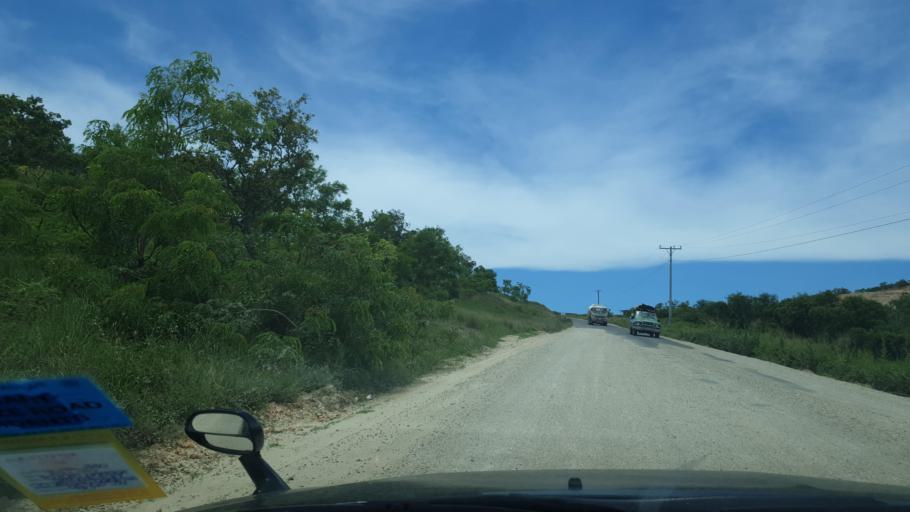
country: PG
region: National Capital
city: Port Moresby
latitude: -9.4359
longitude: 147.0742
